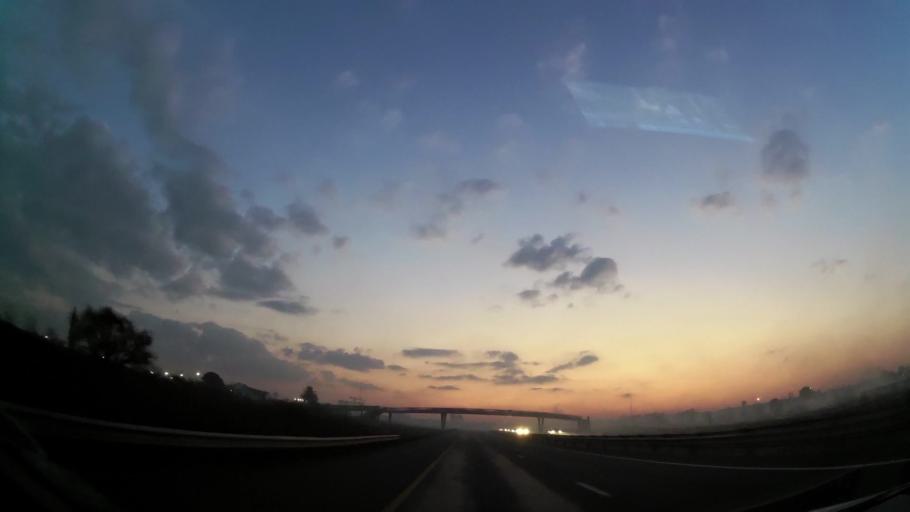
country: ZA
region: Gauteng
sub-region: Ekurhuleni Metropolitan Municipality
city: Springs
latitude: -26.2760
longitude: 28.3828
